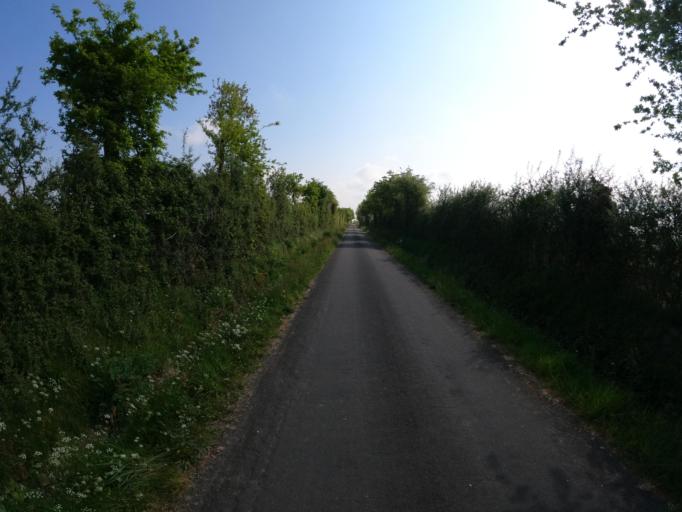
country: FR
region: Pays de la Loire
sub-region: Departement de la Vendee
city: La Bruffiere
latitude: 47.0061
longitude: -1.2188
